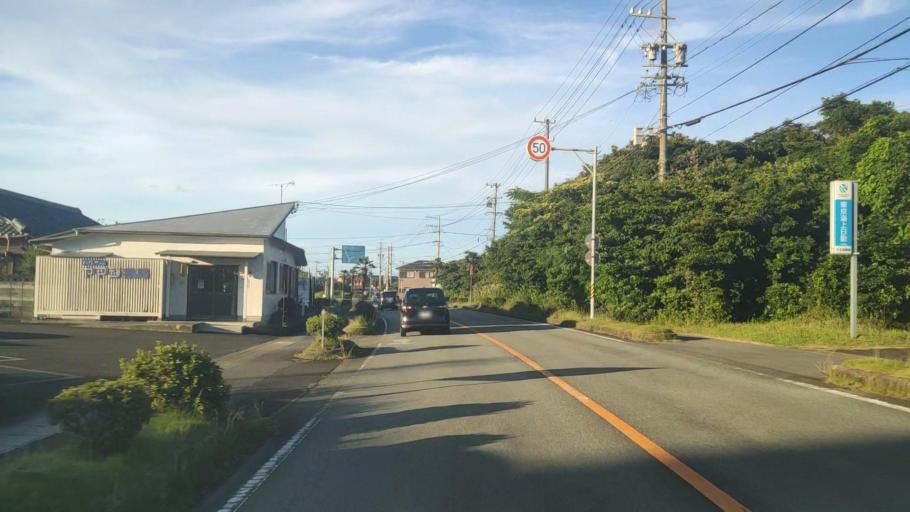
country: JP
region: Mie
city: Toba
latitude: 34.2792
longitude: 136.8797
